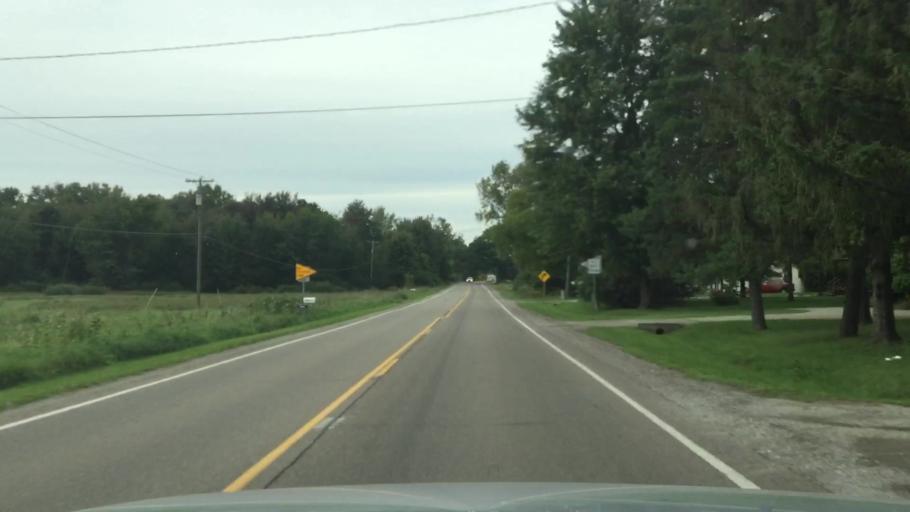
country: US
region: Michigan
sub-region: Genesee County
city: Linden
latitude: 42.8463
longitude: -83.7833
